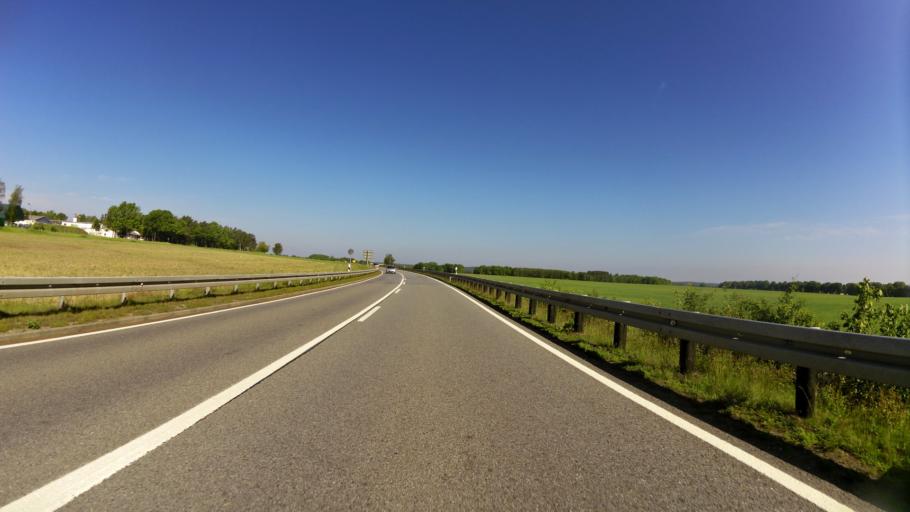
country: DE
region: Saxony
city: Nebelschutz
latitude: 51.2786
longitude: 14.1395
